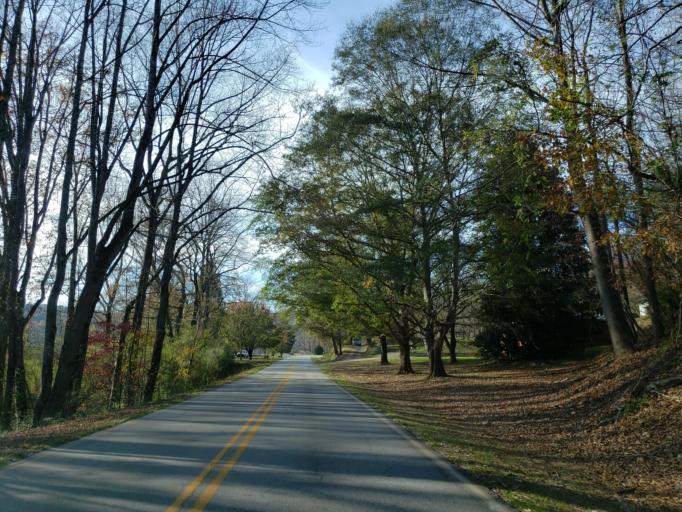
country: US
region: Georgia
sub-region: Lumpkin County
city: Dahlonega
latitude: 34.5863
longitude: -84.0272
